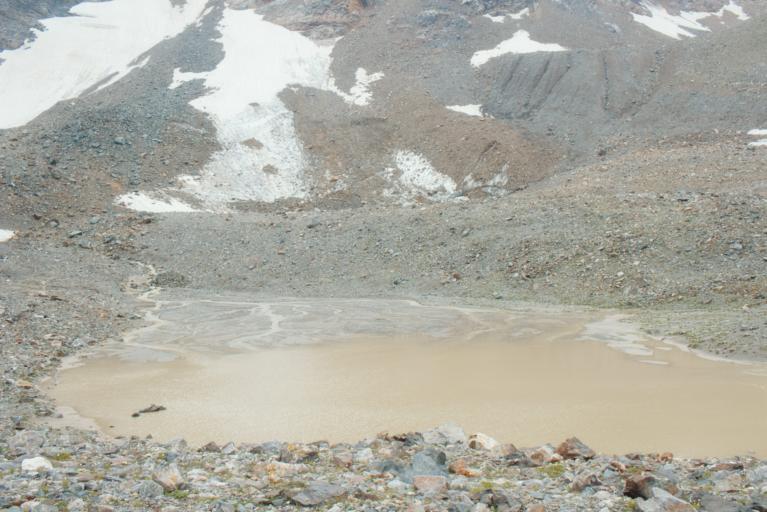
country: RU
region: Karachayevo-Cherkesiya
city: Nizhniy Arkhyz
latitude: 43.4264
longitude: 41.2508
